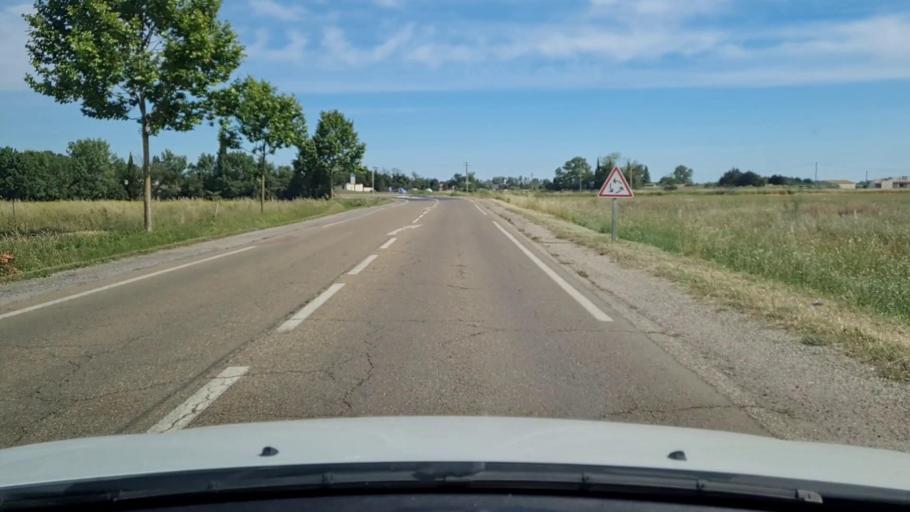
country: FR
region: Languedoc-Roussillon
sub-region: Departement de l'Herault
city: Marsillargues
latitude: 43.6396
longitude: 4.1957
